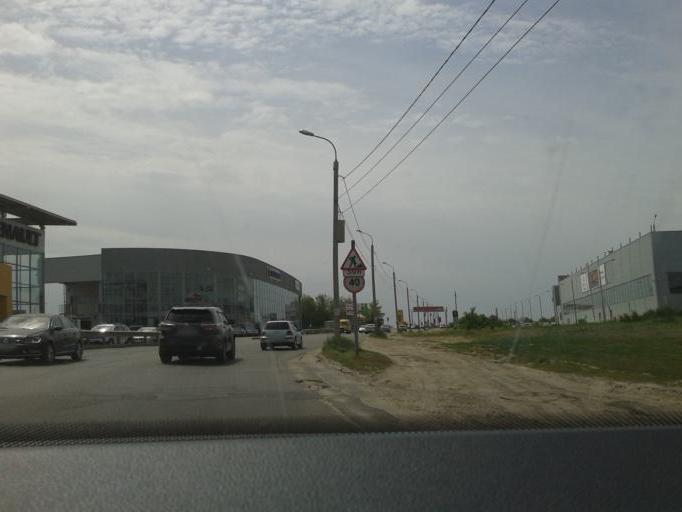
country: RU
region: Volgograd
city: Volgograd
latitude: 48.7509
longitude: 44.5268
